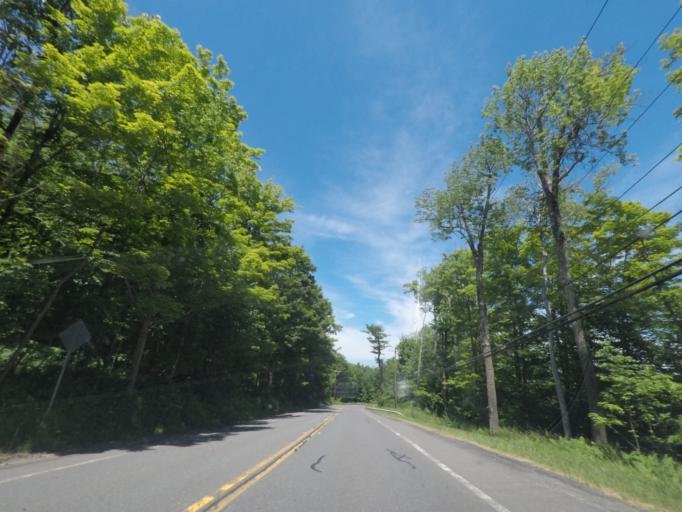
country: US
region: Massachusetts
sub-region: Berkshire County
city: Otis
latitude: 42.2608
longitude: -73.0774
